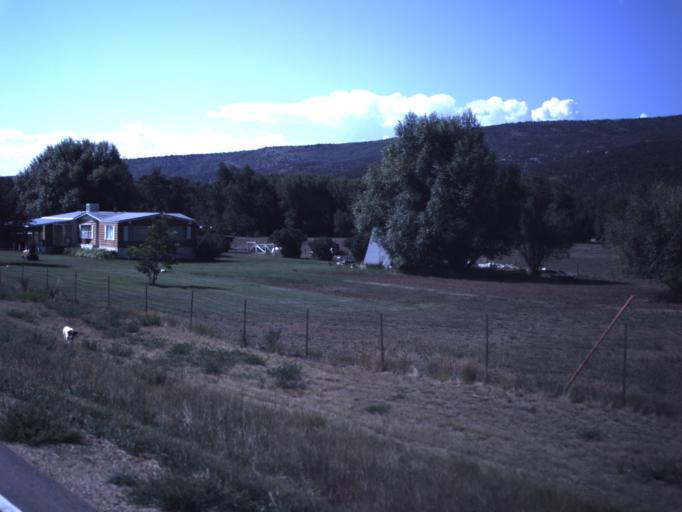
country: US
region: Utah
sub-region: Duchesne County
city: Duchesne
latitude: 40.3670
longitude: -110.7235
